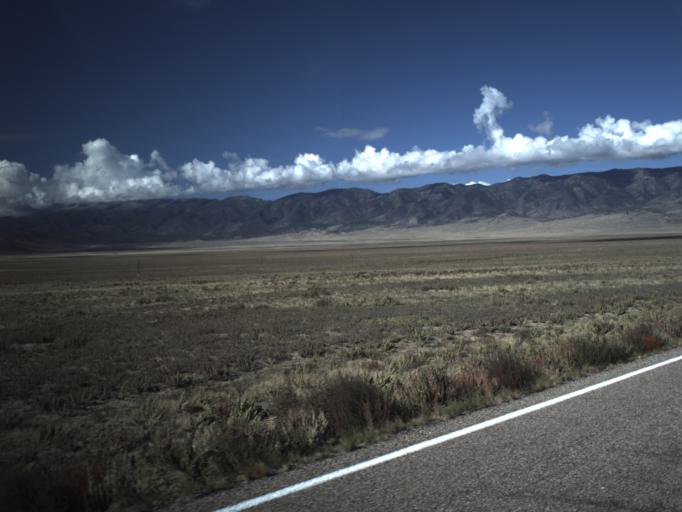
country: US
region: Utah
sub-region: Beaver County
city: Milford
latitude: 38.4563
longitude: -113.3635
